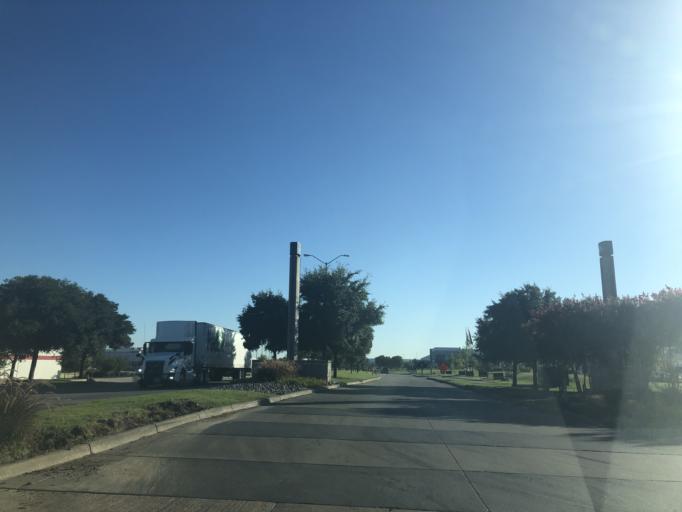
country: US
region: Texas
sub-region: Dallas County
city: Duncanville
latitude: 32.6718
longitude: -96.9695
